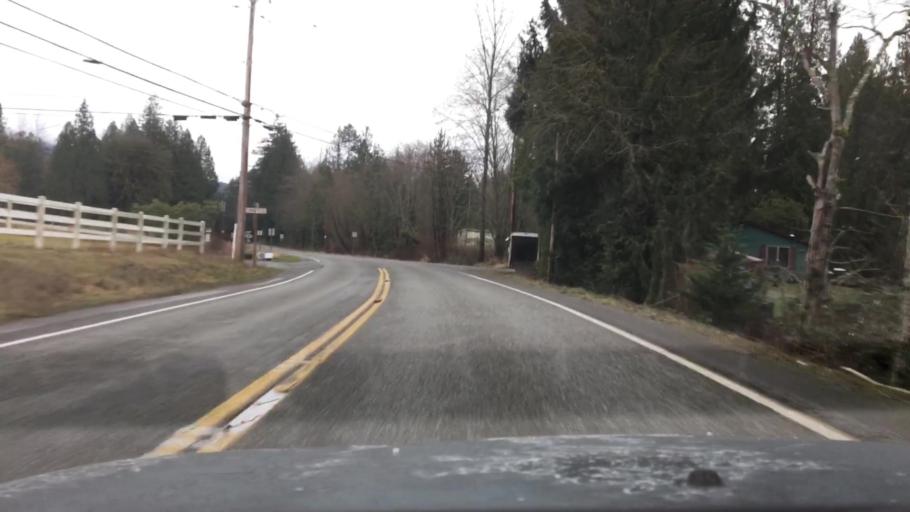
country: US
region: Washington
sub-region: Whatcom County
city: Sudden Valley
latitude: 48.6469
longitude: -122.3242
